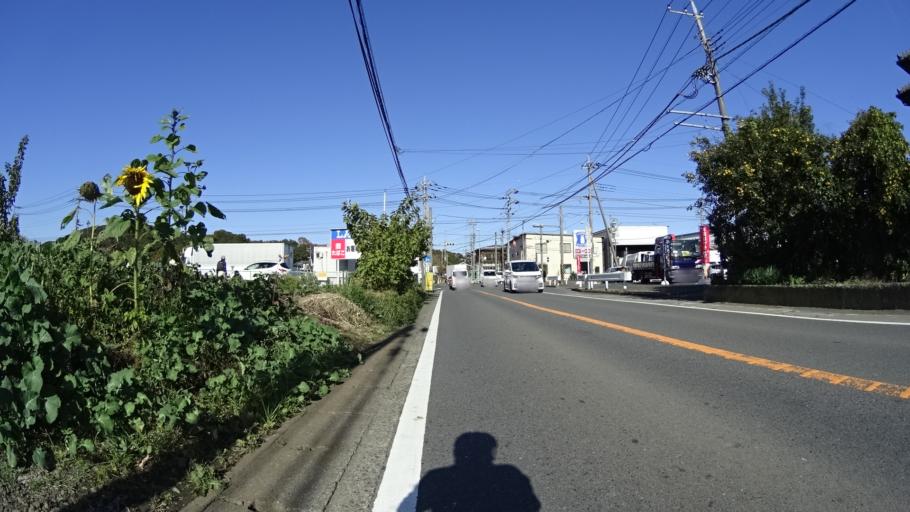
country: JP
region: Kanagawa
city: Zama
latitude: 35.5321
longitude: 139.3202
